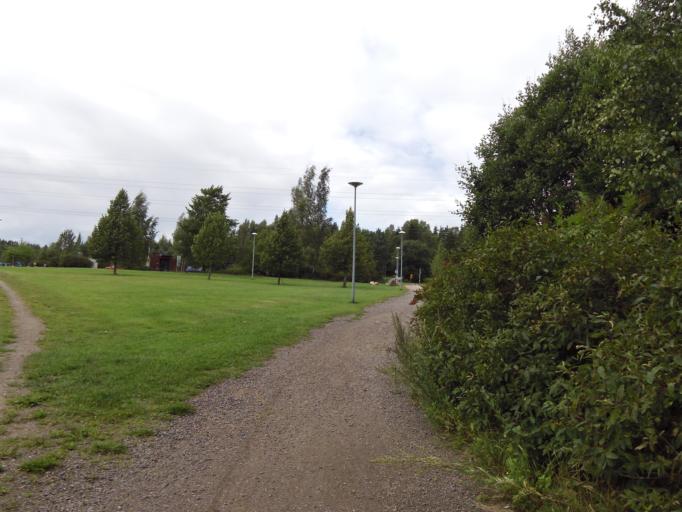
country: FI
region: Uusimaa
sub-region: Helsinki
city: Kauniainen
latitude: 60.1758
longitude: 24.6983
